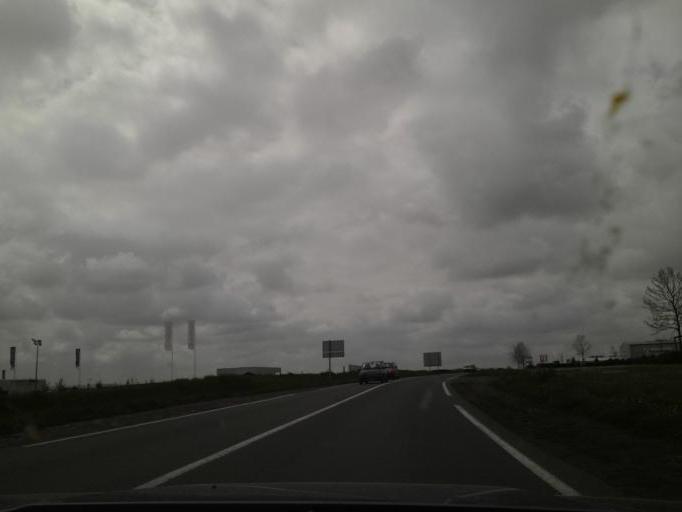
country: FR
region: Pays de la Loire
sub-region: Departement de la Vendee
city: Fontenay-le-Comte
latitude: 46.4467
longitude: -0.8137
